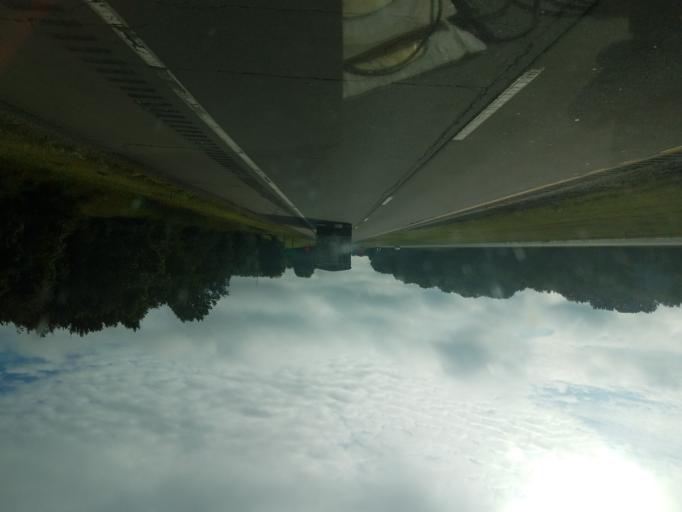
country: US
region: Ohio
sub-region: Richland County
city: Ontario
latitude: 40.7811
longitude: -82.5786
